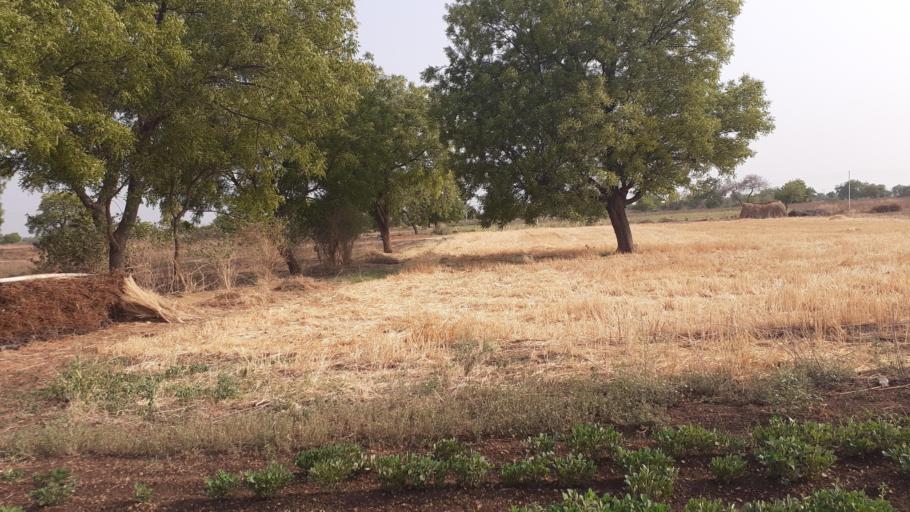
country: IN
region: Maharashtra
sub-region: Buldana
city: Nandura
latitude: 20.8027
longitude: 76.5051
